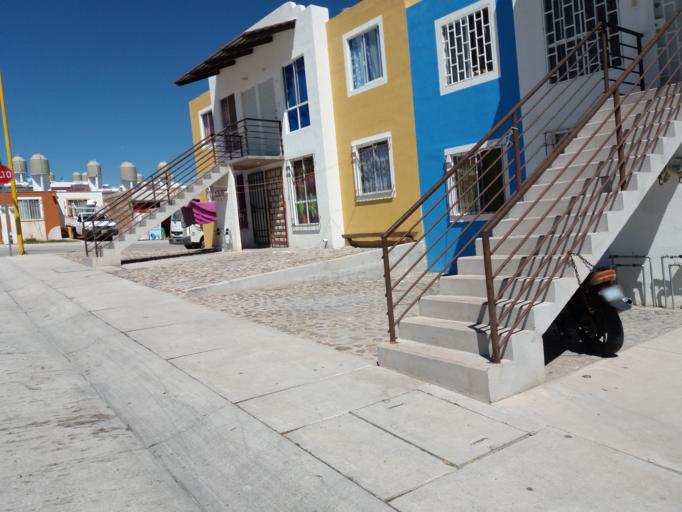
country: MX
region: Aguascalientes
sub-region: Aguascalientes
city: Cumbres III
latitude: 21.8718
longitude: -102.2290
